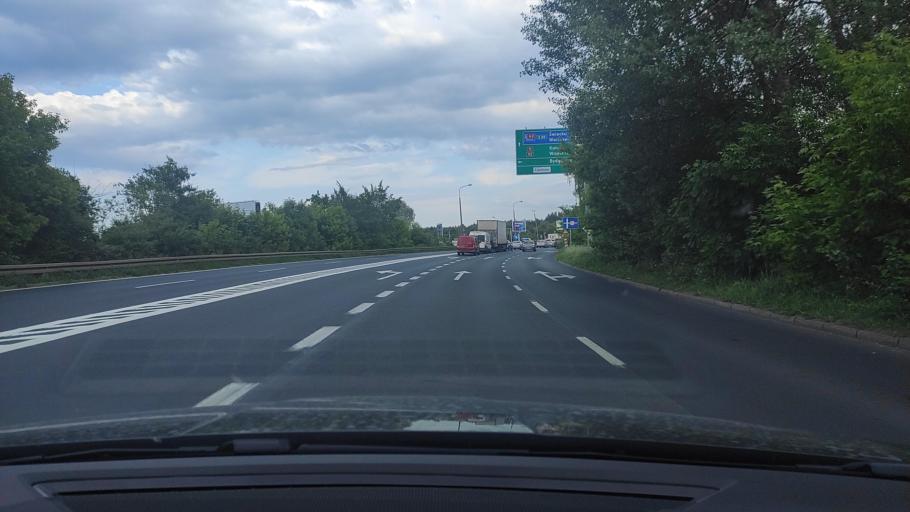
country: PL
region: Greater Poland Voivodeship
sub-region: Powiat poznanski
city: Czerwonak
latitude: 52.4313
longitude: 17.0082
